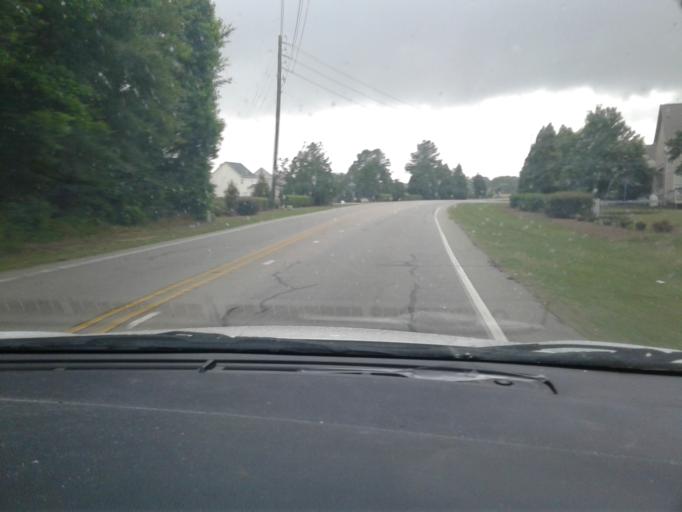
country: US
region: North Carolina
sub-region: Wake County
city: Fuquay-Varina
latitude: 35.6021
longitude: -78.8391
